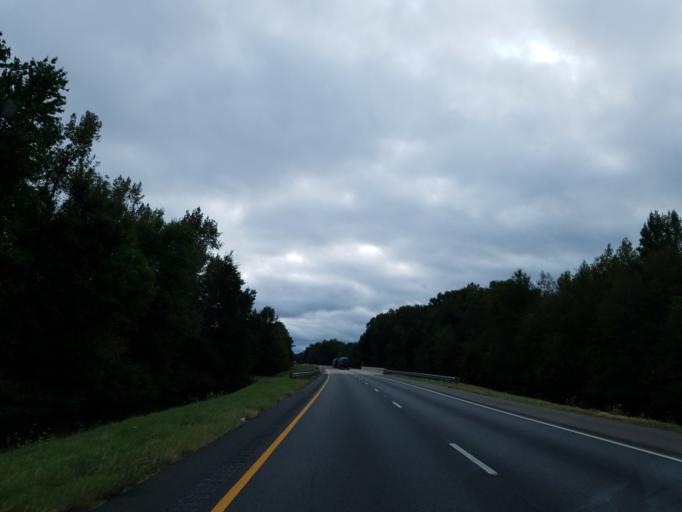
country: US
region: Alabama
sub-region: Tuscaloosa County
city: Tuscaloosa
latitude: 33.1271
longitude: -87.6464
